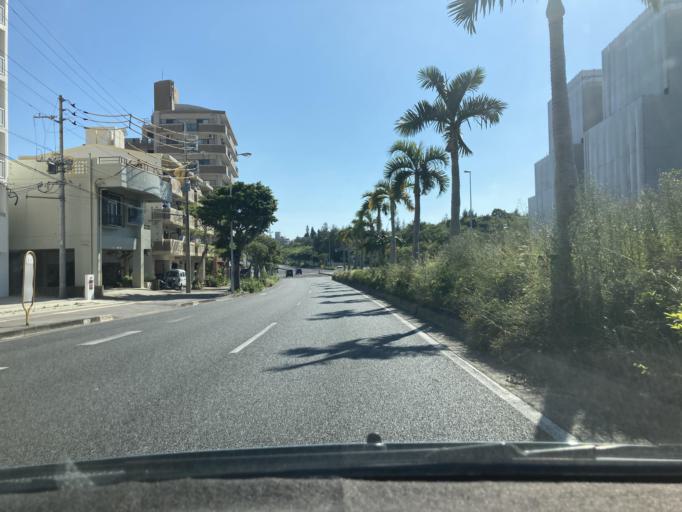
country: JP
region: Okinawa
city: Naha-shi
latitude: 26.2037
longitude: 127.6625
